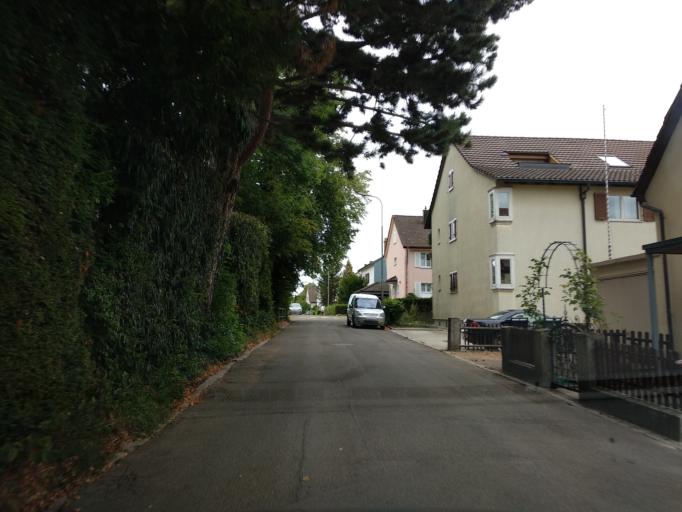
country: CH
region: Schaffhausen
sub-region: Bezirk Schaffhausen
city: Schaffhausen
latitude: 47.7141
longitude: 8.6463
